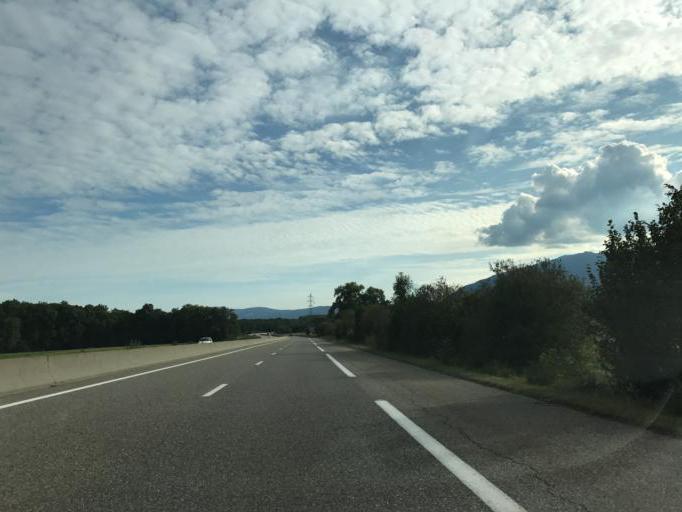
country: FR
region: Rhone-Alpes
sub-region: Departement de l'Ain
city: Saint-Jean-de-Gonville
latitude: 46.2098
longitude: 5.9703
